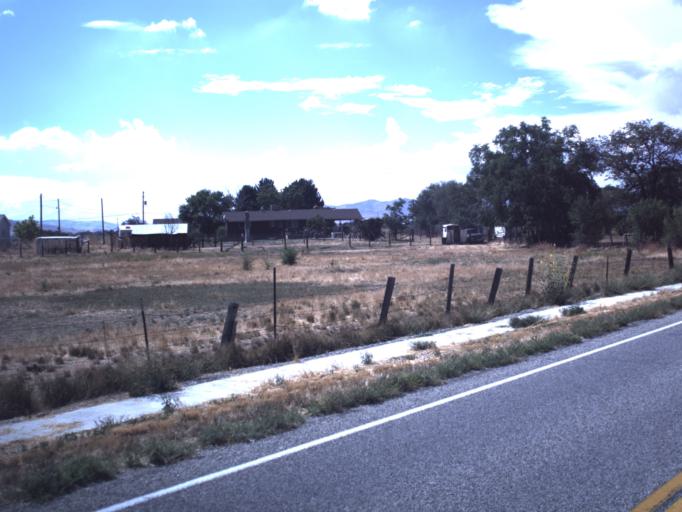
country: US
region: Utah
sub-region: Box Elder County
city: Honeyville
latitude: 41.6439
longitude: -112.0826
